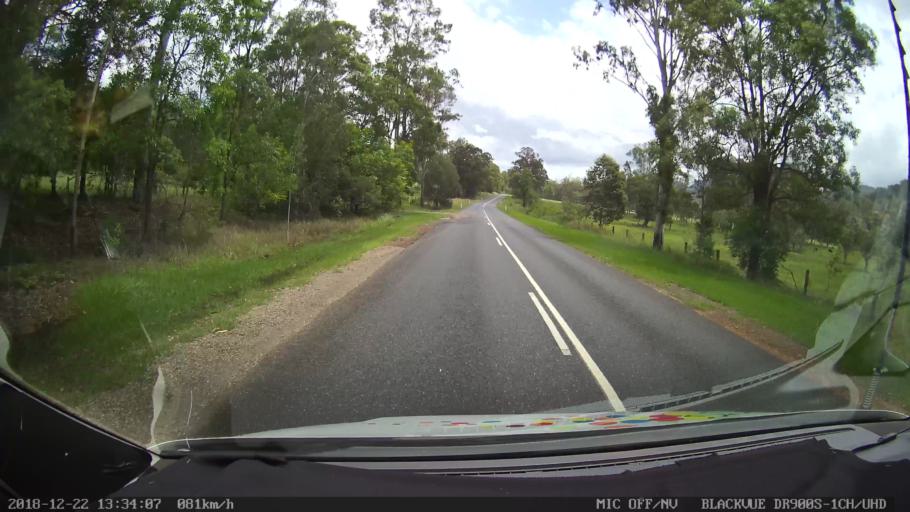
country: AU
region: New South Wales
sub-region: Clarence Valley
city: Coutts Crossing
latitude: -29.8678
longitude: 152.8210
